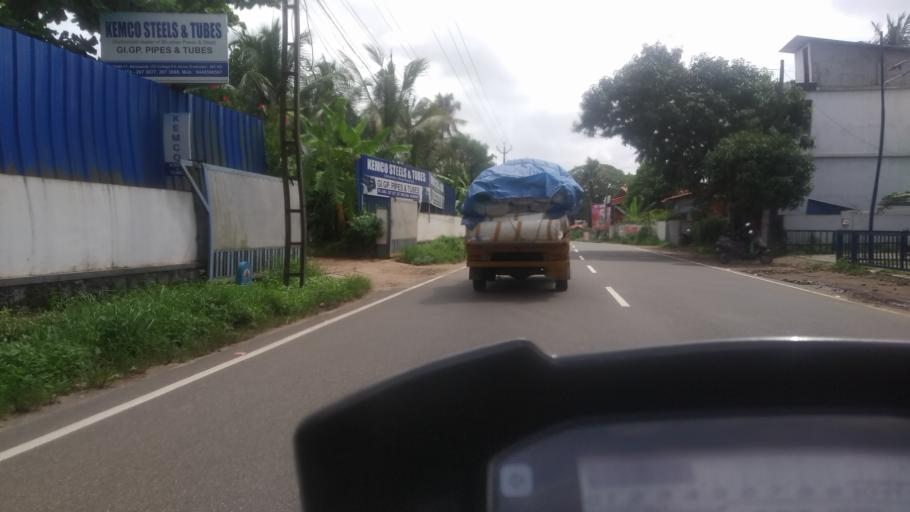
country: IN
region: Kerala
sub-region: Ernakulam
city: Aluva
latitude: 10.1261
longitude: 76.3183
